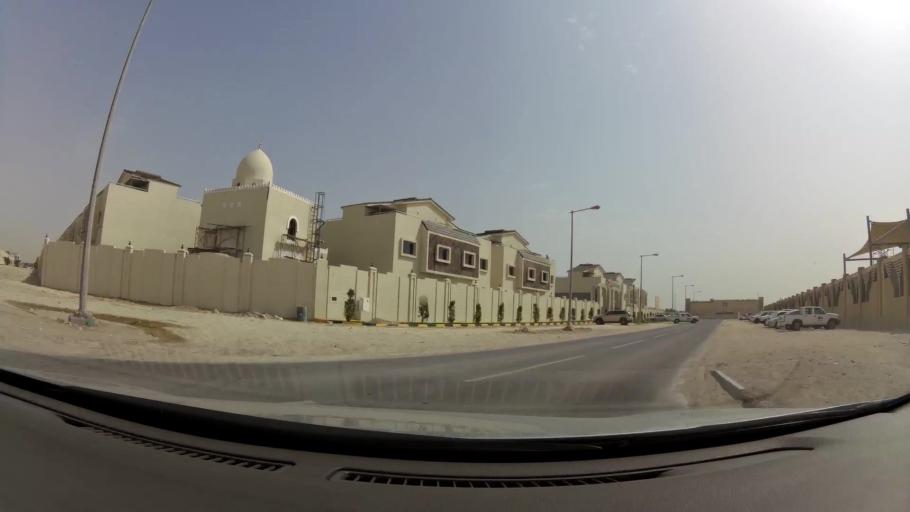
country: QA
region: Baladiyat ad Dawhah
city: Doha
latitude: 25.3011
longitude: 51.4834
